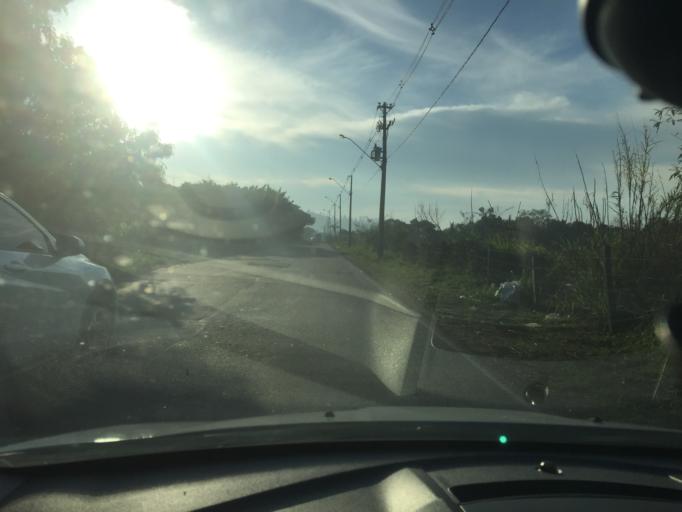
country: BR
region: Sao Paulo
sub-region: Varzea Paulista
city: Varzea Paulista
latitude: -23.2028
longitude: -46.8575
